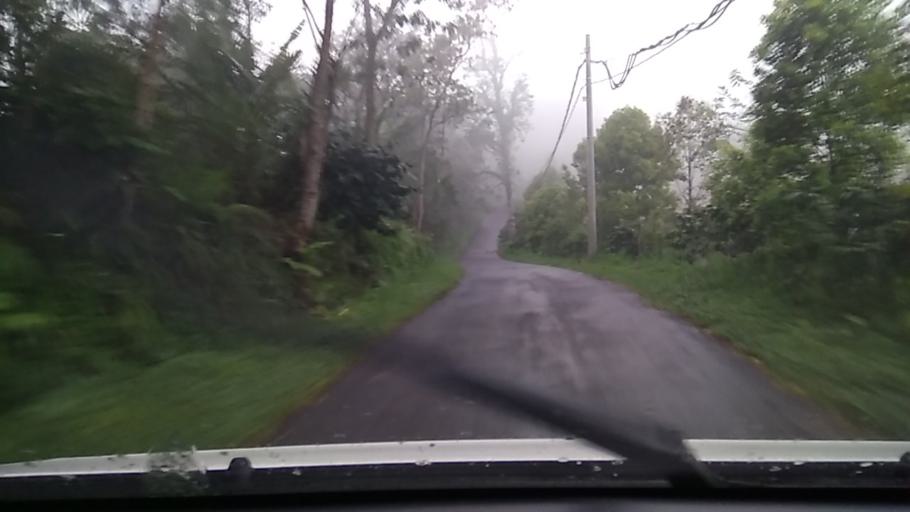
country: ID
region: Bali
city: Banjar Ambengan
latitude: -8.2007
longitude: 115.1762
